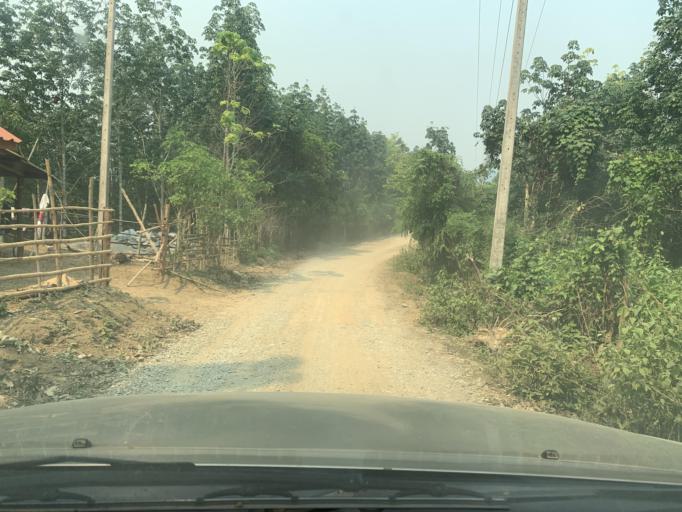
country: LA
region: Louangphabang
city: Louangphabang
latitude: 19.8953
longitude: 102.2529
